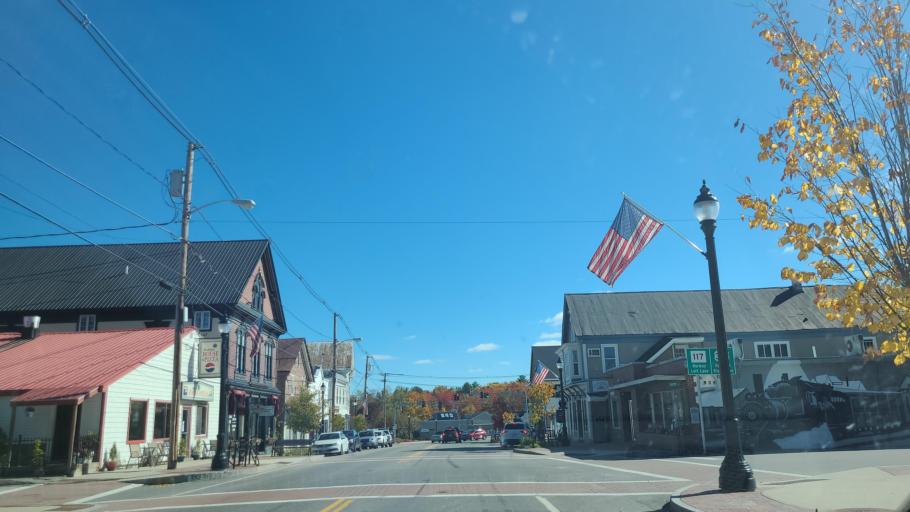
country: US
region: Maine
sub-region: Cumberland County
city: Bridgton
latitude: 44.0542
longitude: -70.7031
